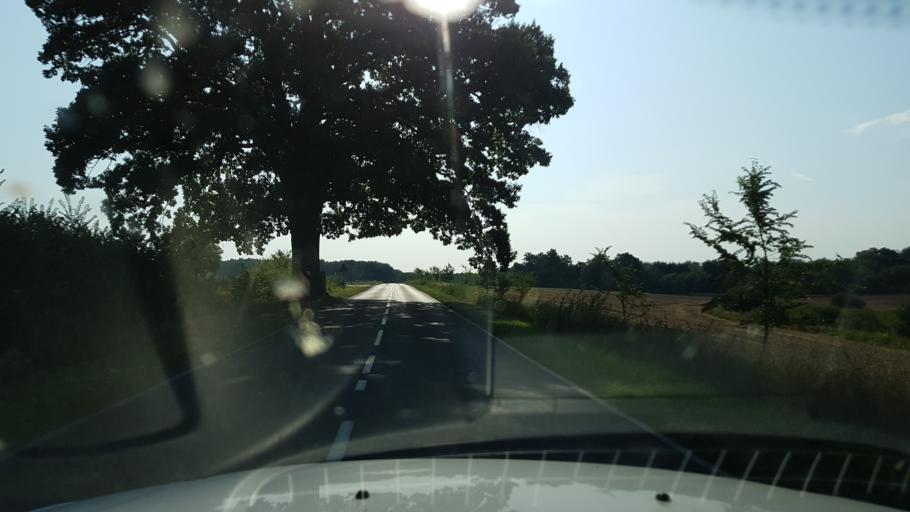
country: PL
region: West Pomeranian Voivodeship
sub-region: Powiat lobeski
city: Resko
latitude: 53.7747
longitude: 15.4350
